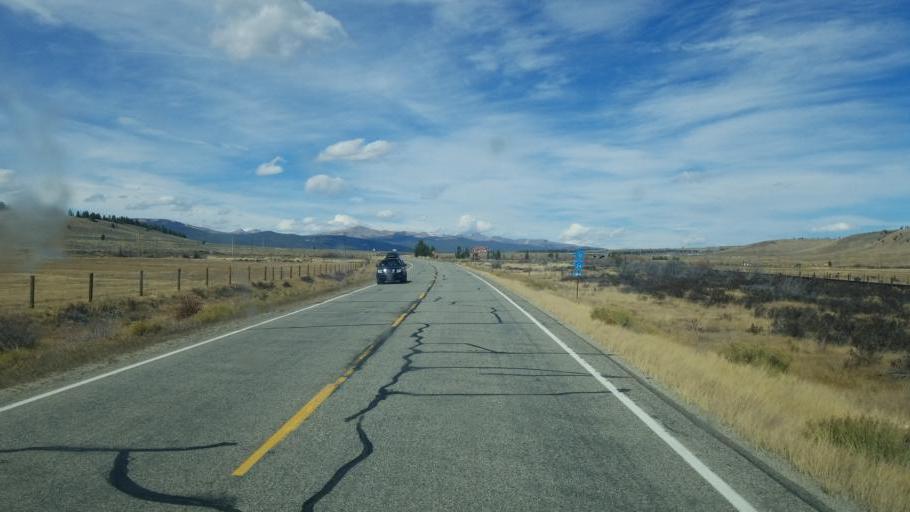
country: US
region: Colorado
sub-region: Lake County
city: Leadville
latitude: 39.1586
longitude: -106.3237
